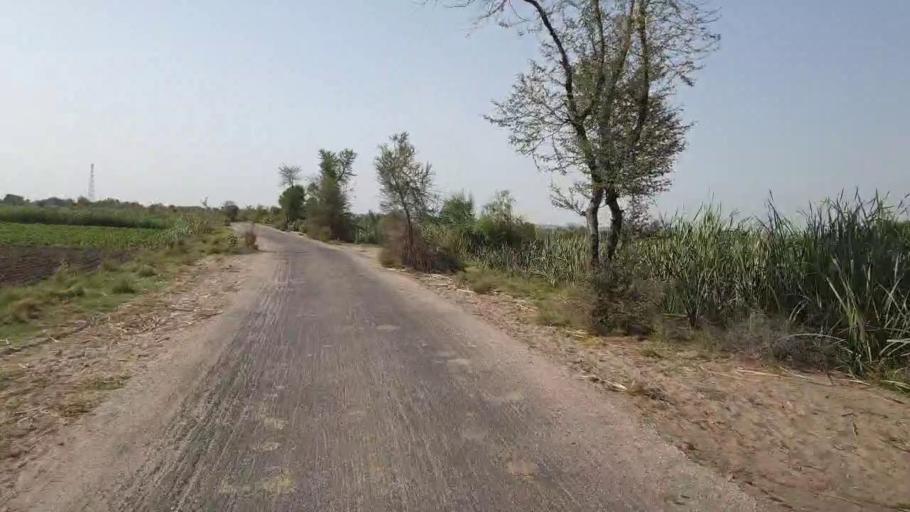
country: PK
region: Sindh
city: Kandiari
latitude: 26.7034
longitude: 68.9644
